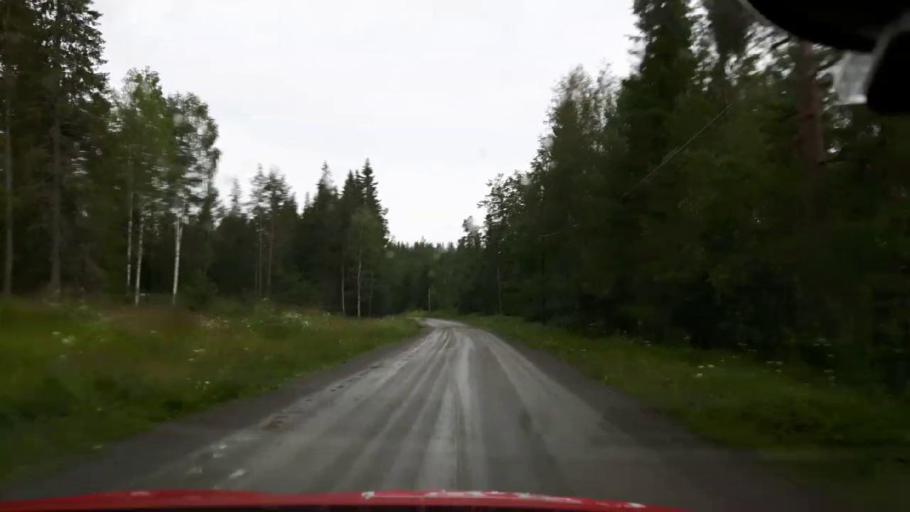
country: SE
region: Jaemtland
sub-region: OEstersunds Kommun
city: Brunflo
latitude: 62.9041
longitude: 14.8589
